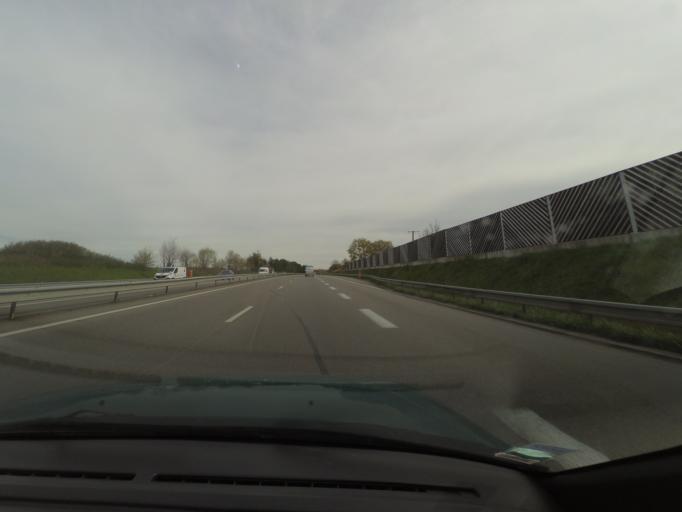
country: FR
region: Pays de la Loire
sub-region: Departement de la Loire-Atlantique
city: Mauves-sur-Loire
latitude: 47.3229
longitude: -1.4067
